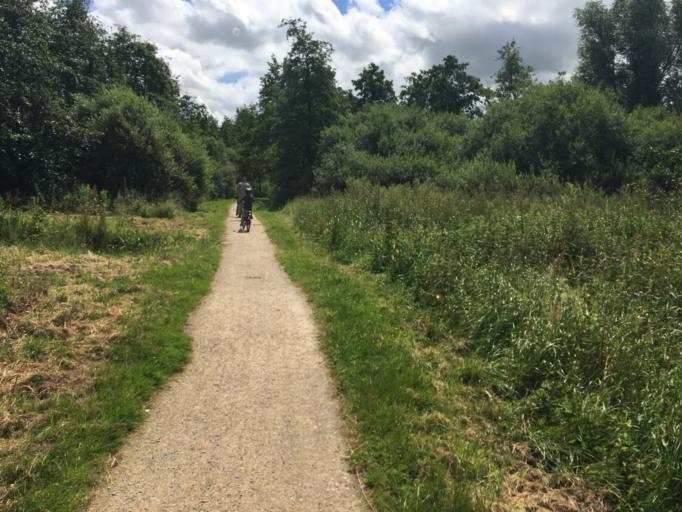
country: NL
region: South Holland
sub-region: Gemeente Gouda
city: Gouda
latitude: 52.0200
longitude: 4.7344
